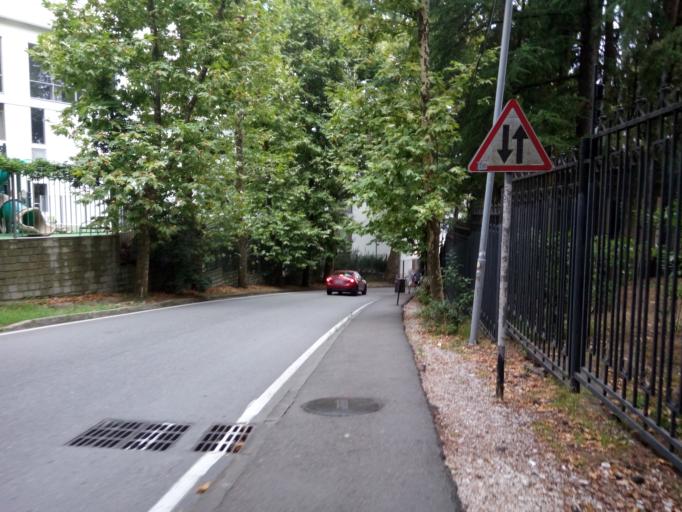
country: RU
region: Krasnodarskiy
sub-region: Sochi City
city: Sochi
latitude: 43.5631
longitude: 39.7613
